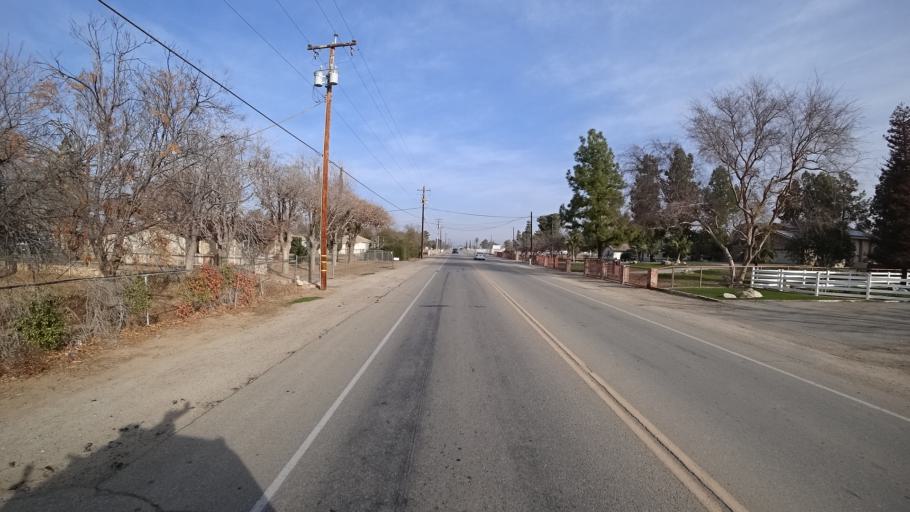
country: US
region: California
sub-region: Kern County
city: Lamont
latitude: 35.3270
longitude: -118.9320
